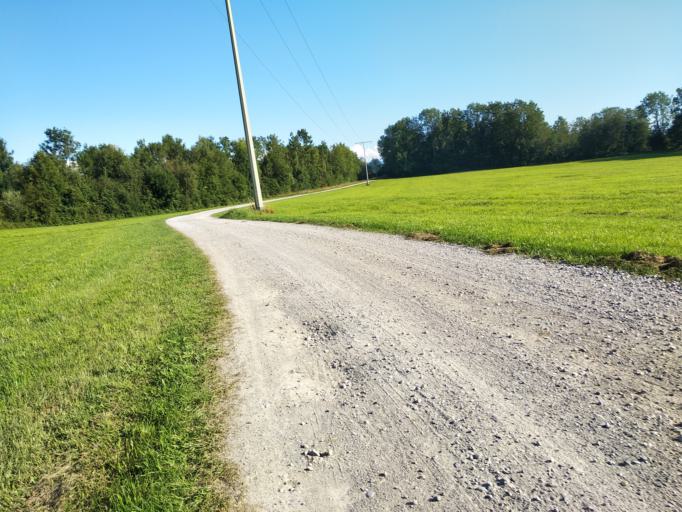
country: DE
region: Baden-Wuerttemberg
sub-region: Tuebingen Region
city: Leutkirch im Allgau
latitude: 47.7700
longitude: 10.0442
